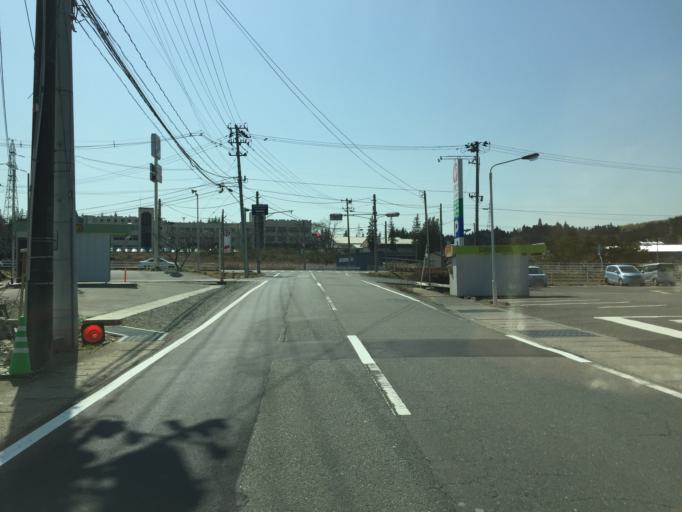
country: JP
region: Fukushima
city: Iwaki
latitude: 37.0068
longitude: 140.7405
